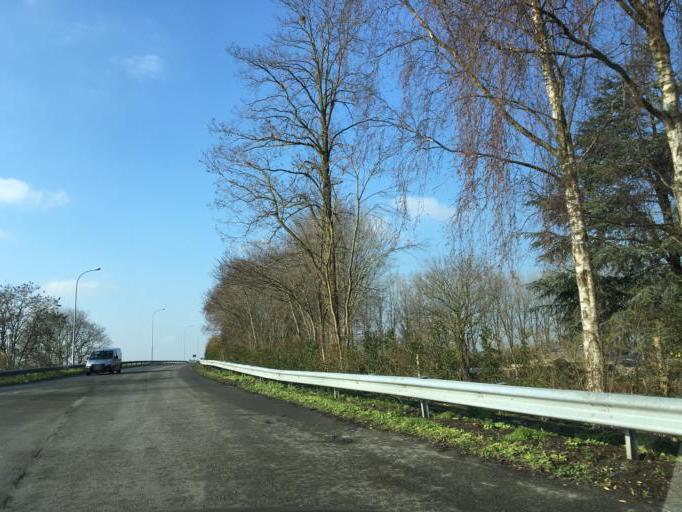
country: BE
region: Flanders
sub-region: Provincie West-Vlaanderen
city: Ardooie
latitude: 50.9444
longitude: 3.1773
